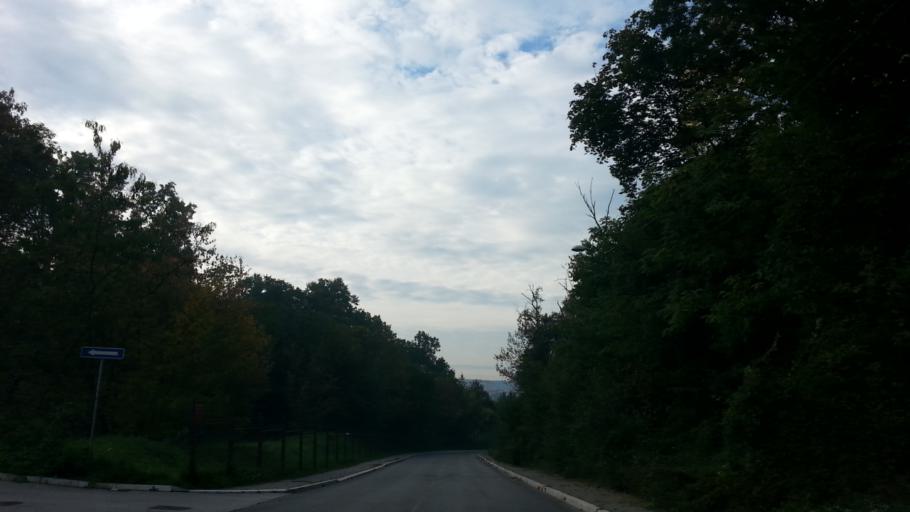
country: RS
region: Central Serbia
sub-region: Belgrade
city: Savski Venac
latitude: 44.7624
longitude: 20.4568
